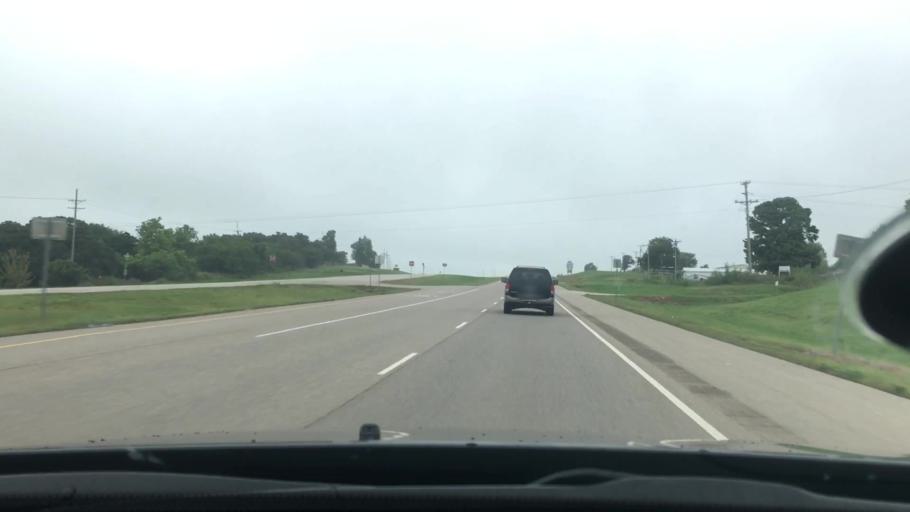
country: US
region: Oklahoma
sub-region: Seminole County
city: Seminole
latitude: 35.3036
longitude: -96.6707
